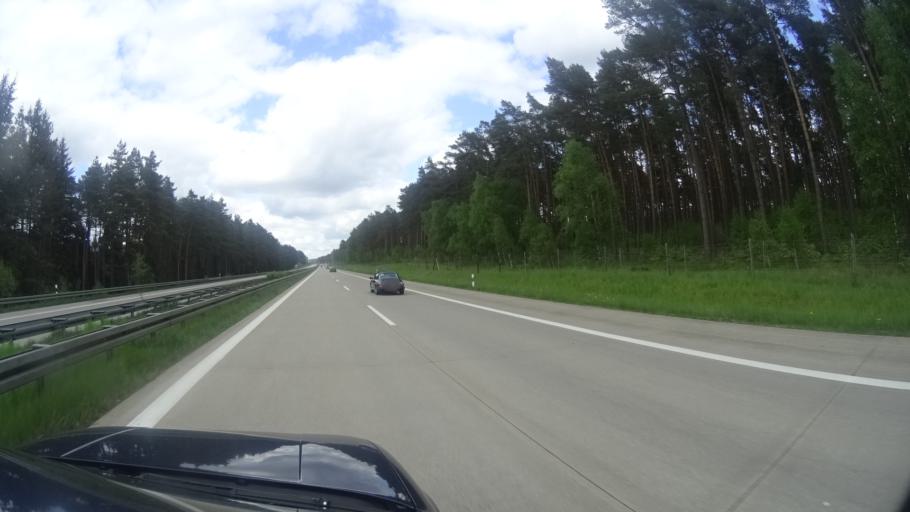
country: DE
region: Mecklenburg-Vorpommern
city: Krakow am See
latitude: 53.5789
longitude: 12.3309
